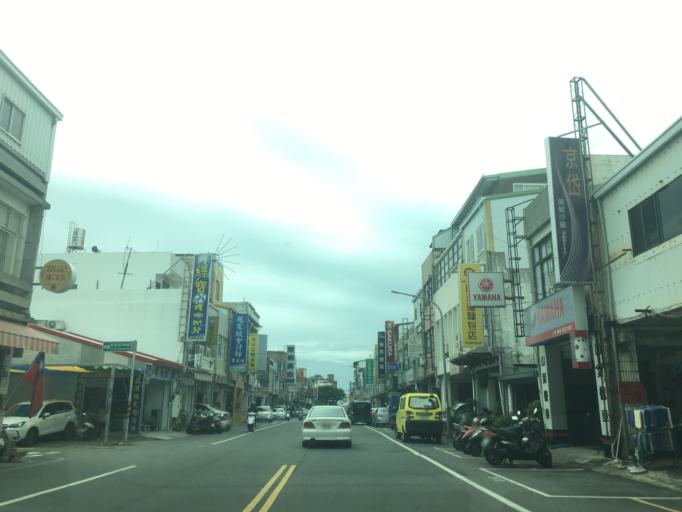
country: TW
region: Taiwan
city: Taitung City
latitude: 22.7587
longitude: 121.1410
